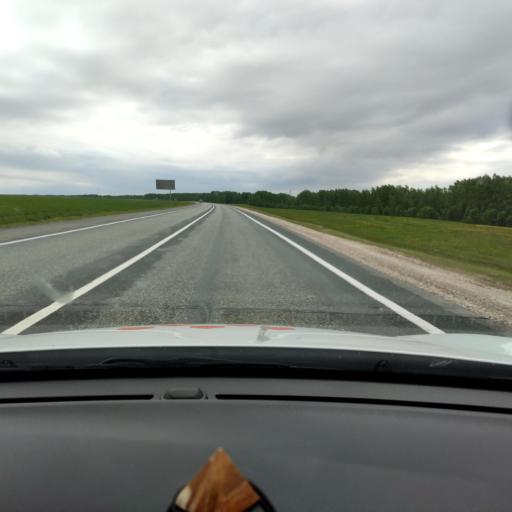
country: RU
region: Tatarstan
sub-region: Alekseyevskiy Rayon
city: Alekseyevskoye
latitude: 55.3951
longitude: 49.8728
